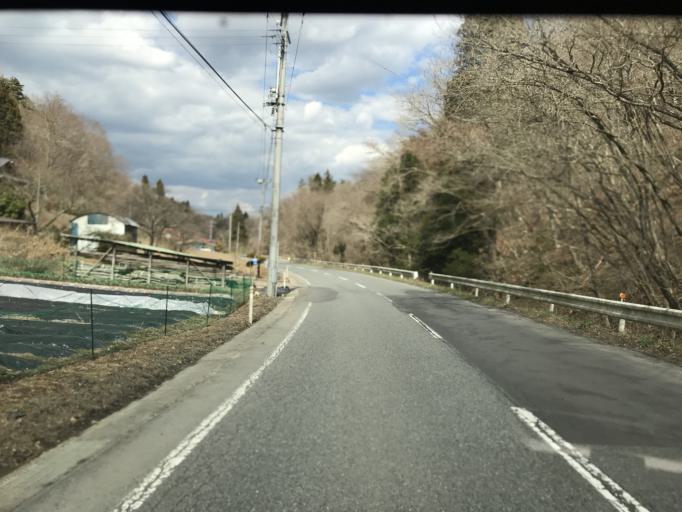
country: JP
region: Iwate
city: Ichinoseki
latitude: 38.8264
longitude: 141.3312
